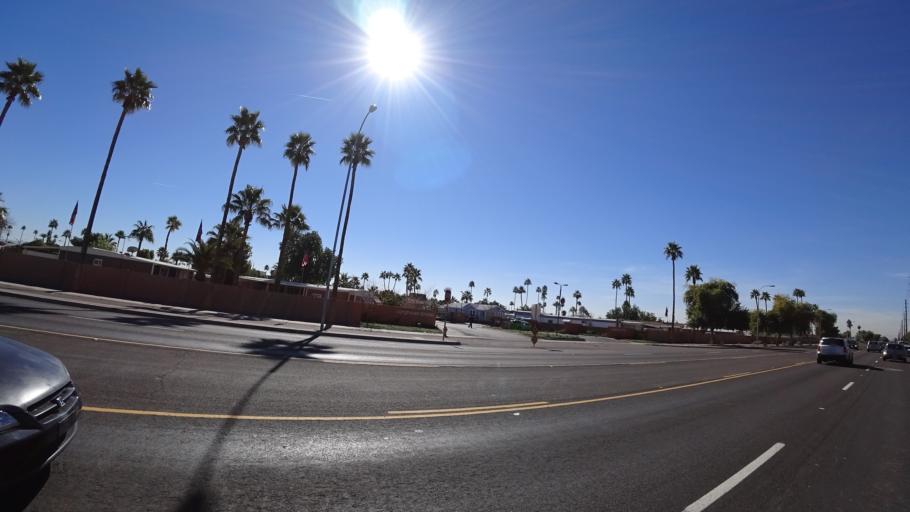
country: US
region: Arizona
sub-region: Maricopa County
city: Glendale
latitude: 33.5095
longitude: -112.1705
